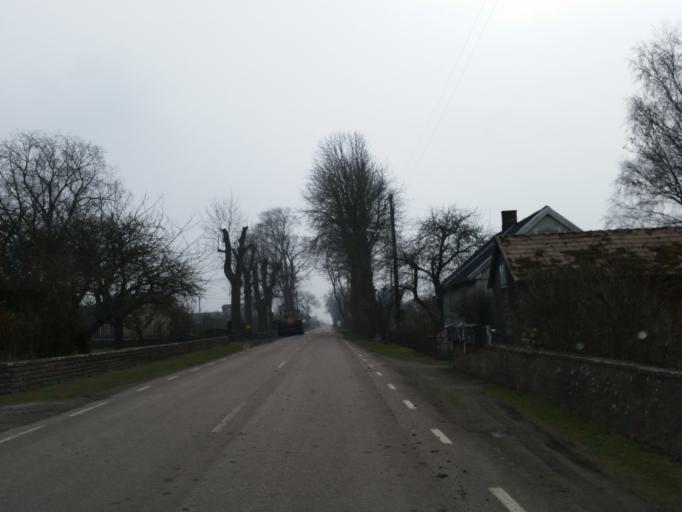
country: SE
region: Kalmar
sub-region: Morbylanga Kommun
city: Moerbylanga
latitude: 56.3917
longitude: 16.4132
